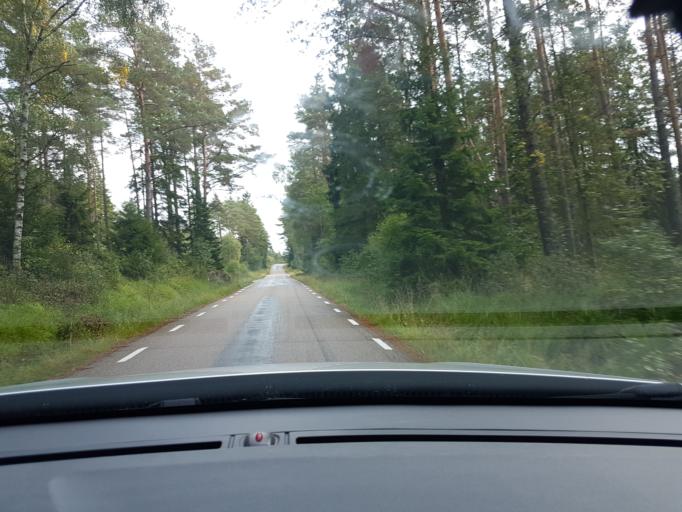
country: SE
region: Vaestra Goetaland
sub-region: Ale Kommun
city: Alvangen
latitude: 57.9074
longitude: 12.1699
